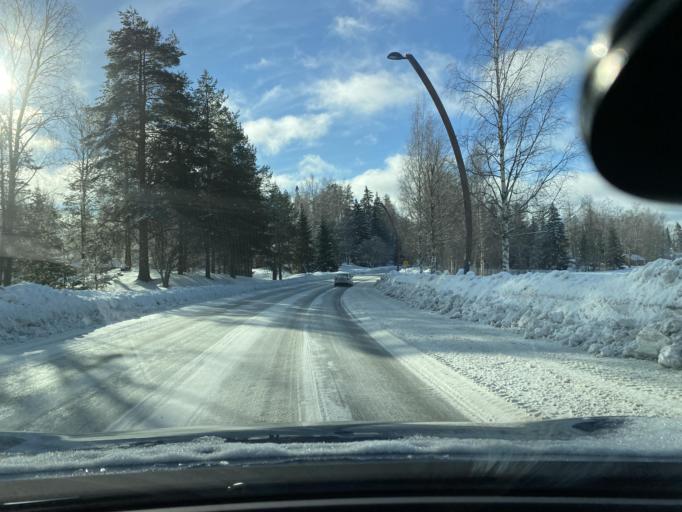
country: FI
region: Southern Savonia
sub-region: Mikkeli
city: Kangasniemi
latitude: 61.9946
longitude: 26.6476
